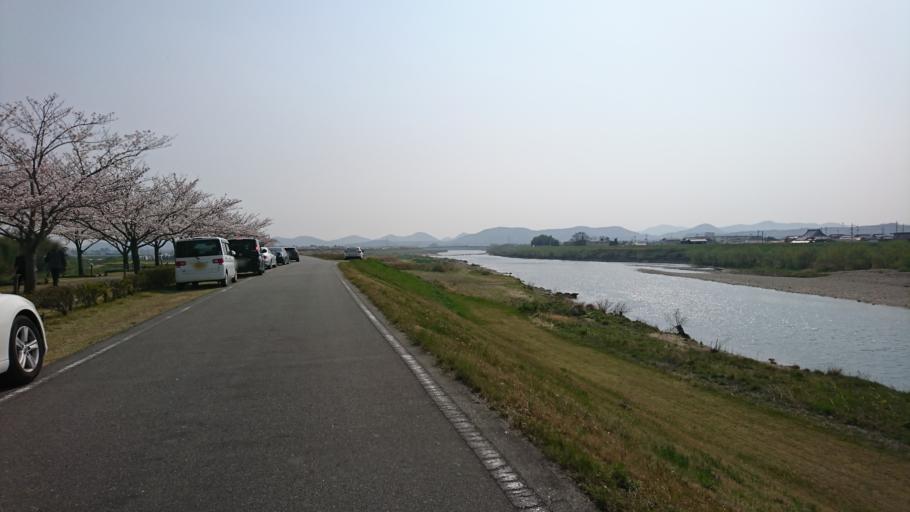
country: JP
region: Hyogo
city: Ono
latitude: 34.8742
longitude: 134.9267
